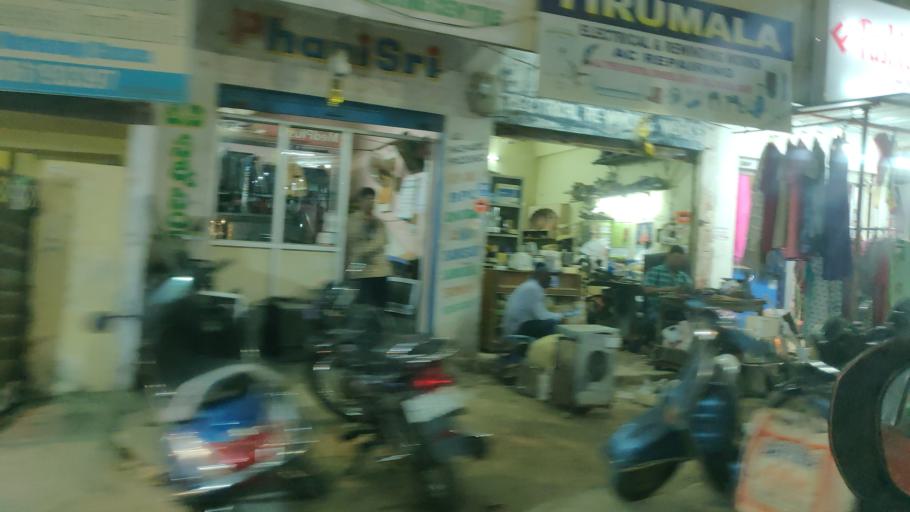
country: IN
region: Telangana
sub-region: Medak
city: Serilingampalle
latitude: 17.4942
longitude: 78.3225
